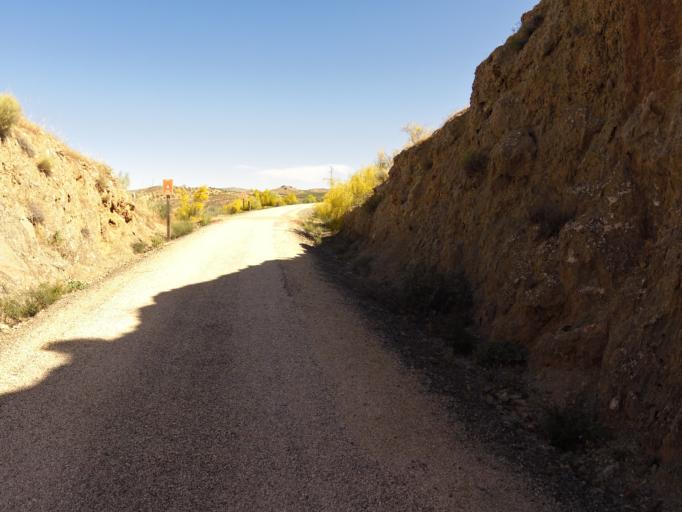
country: ES
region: Andalusia
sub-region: Provincia de Jaen
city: Alcaudete
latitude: 37.6017
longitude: -4.1585
